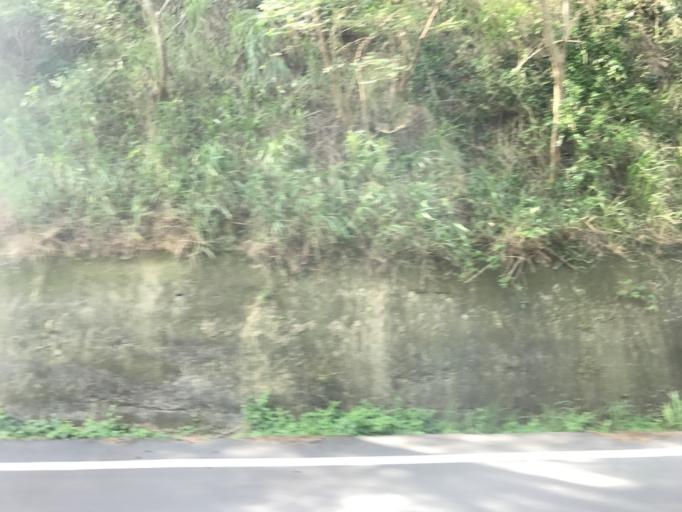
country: TW
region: Taiwan
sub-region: Hsinchu
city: Hsinchu
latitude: 24.7635
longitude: 120.9506
